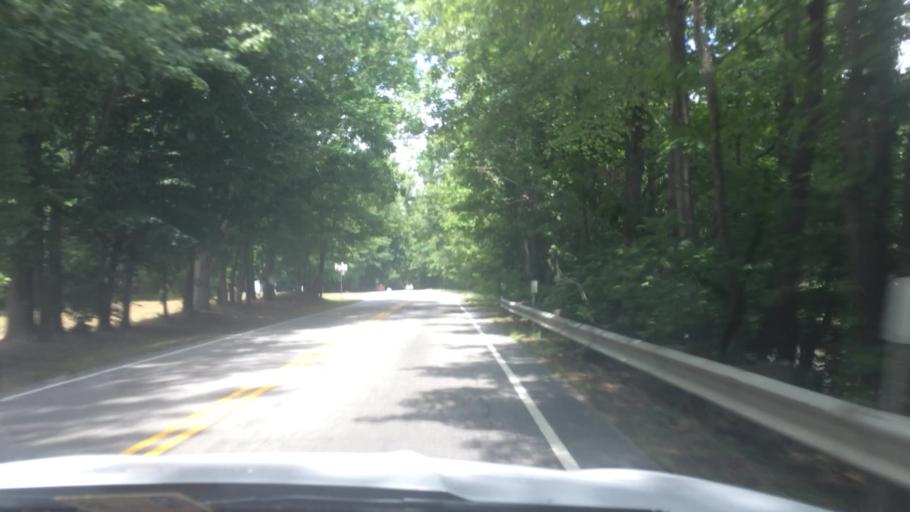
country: US
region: Virginia
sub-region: York County
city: Yorktown
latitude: 37.2036
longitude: -76.5808
